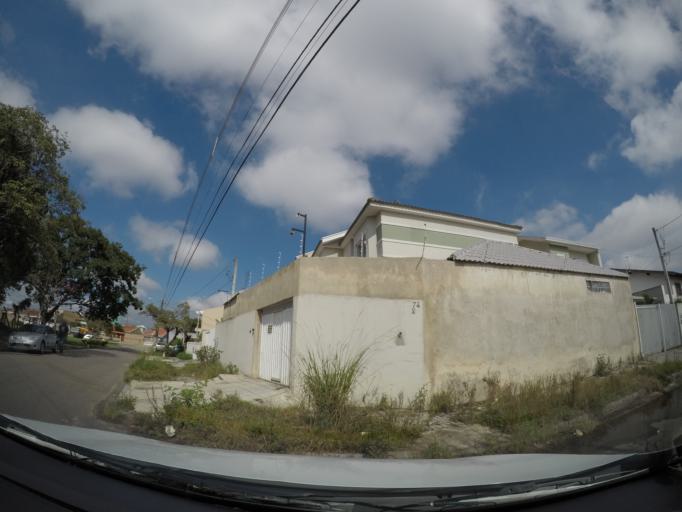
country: BR
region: Parana
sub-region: Sao Jose Dos Pinhais
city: Sao Jose dos Pinhais
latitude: -25.4955
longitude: -49.2231
